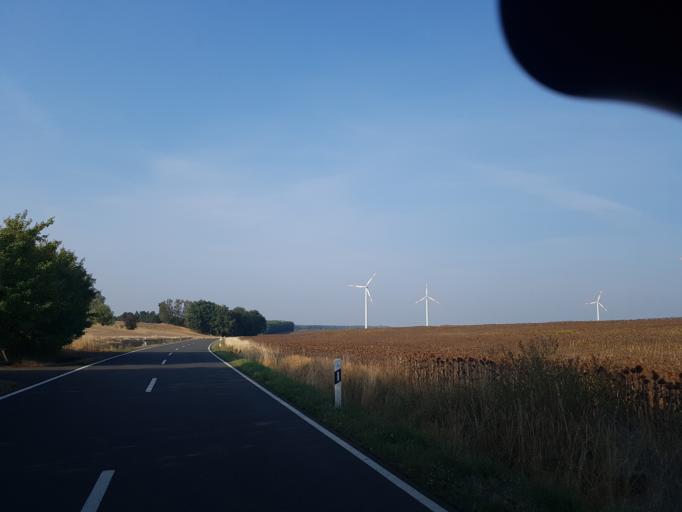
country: DE
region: Saxony-Anhalt
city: Nudersdorf
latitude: 51.9646
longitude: 12.6325
